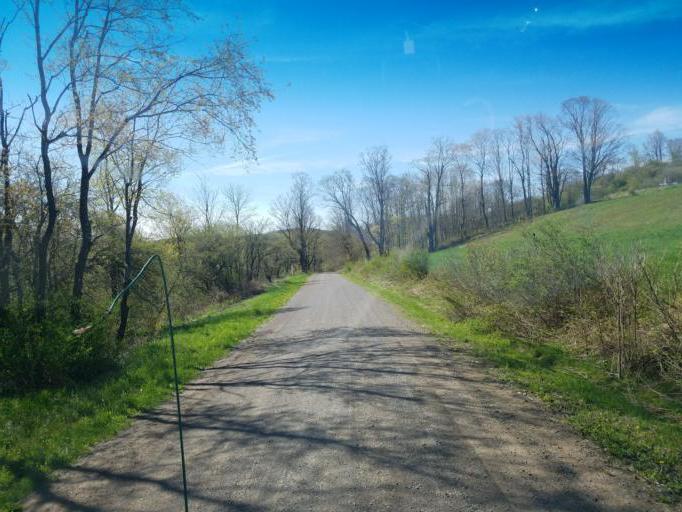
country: US
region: New York
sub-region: Allegany County
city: Andover
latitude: 41.9599
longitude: -77.7809
